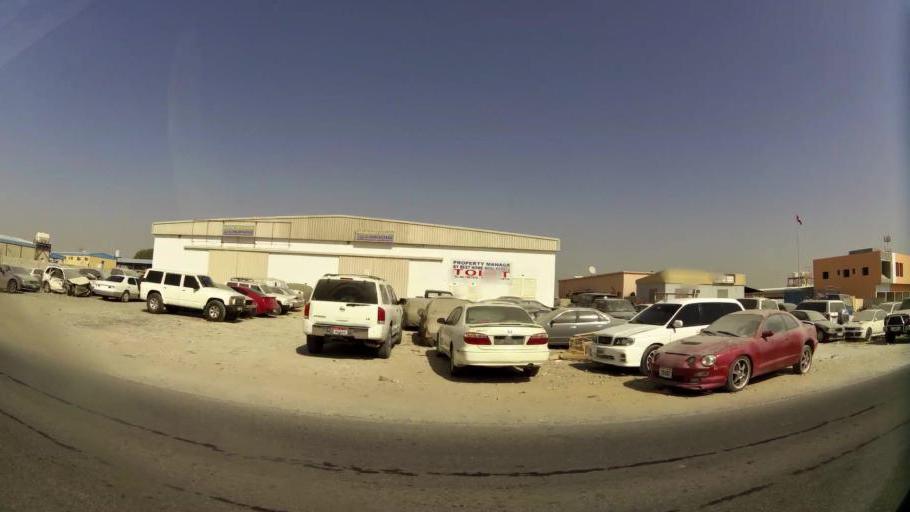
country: AE
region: Ajman
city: Ajman
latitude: 25.4340
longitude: 55.5368
